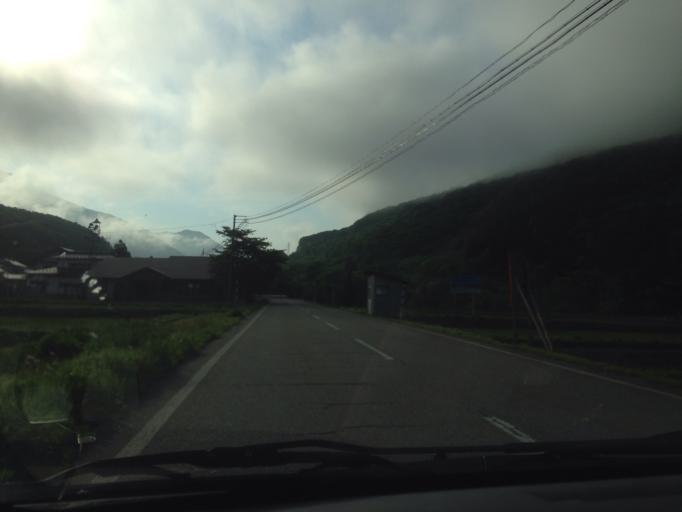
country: JP
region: Fukushima
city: Inawashiro
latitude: 37.3082
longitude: 139.9085
